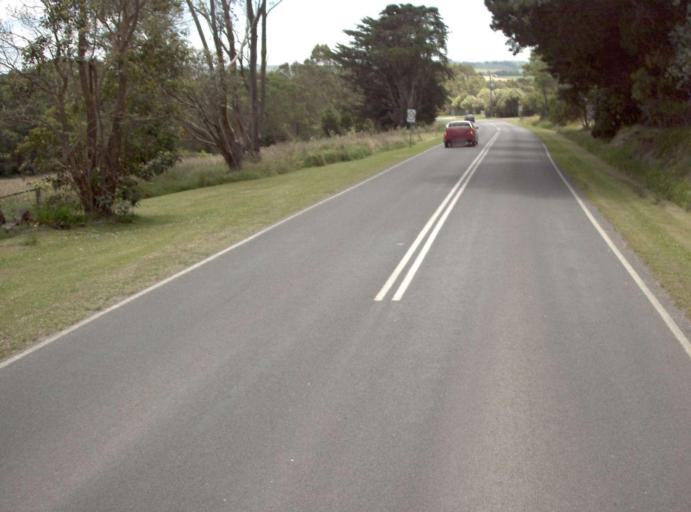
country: AU
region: Victoria
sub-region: Bass Coast
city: North Wonthaggi
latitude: -38.7013
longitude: 146.0875
